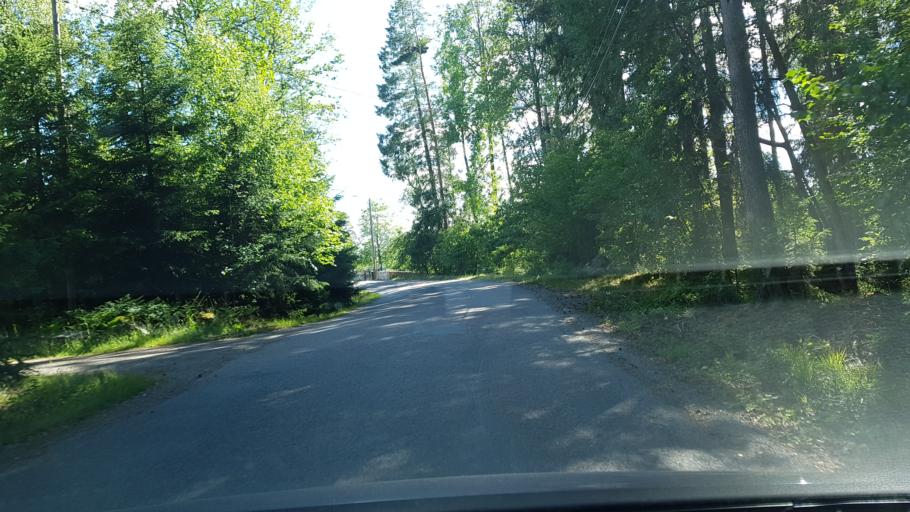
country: SE
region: Stockholm
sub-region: Upplands-Bro Kommun
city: Kungsaengen
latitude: 59.4982
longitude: 17.8069
